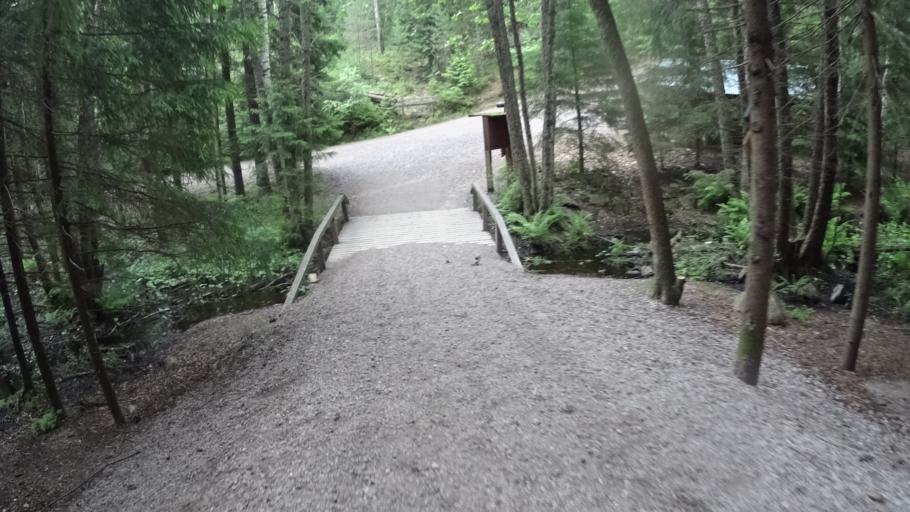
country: FI
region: Uusimaa
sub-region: Helsinki
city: Espoo
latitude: 60.3062
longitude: 24.5109
